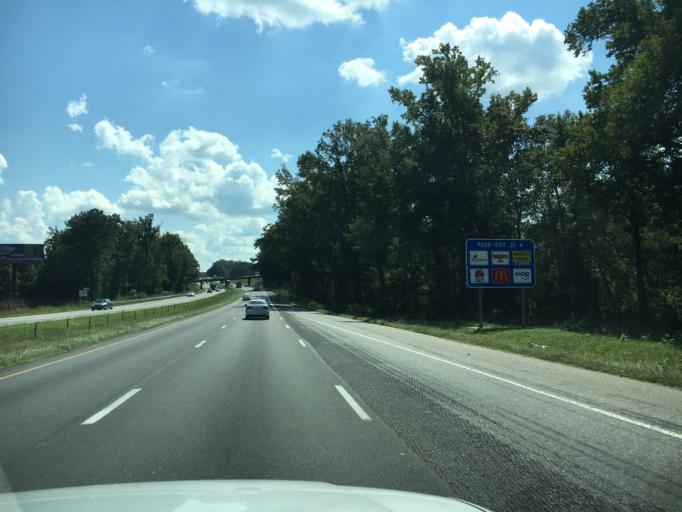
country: US
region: South Carolina
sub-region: Spartanburg County
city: Fairforest
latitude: 34.9649
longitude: -82.0057
